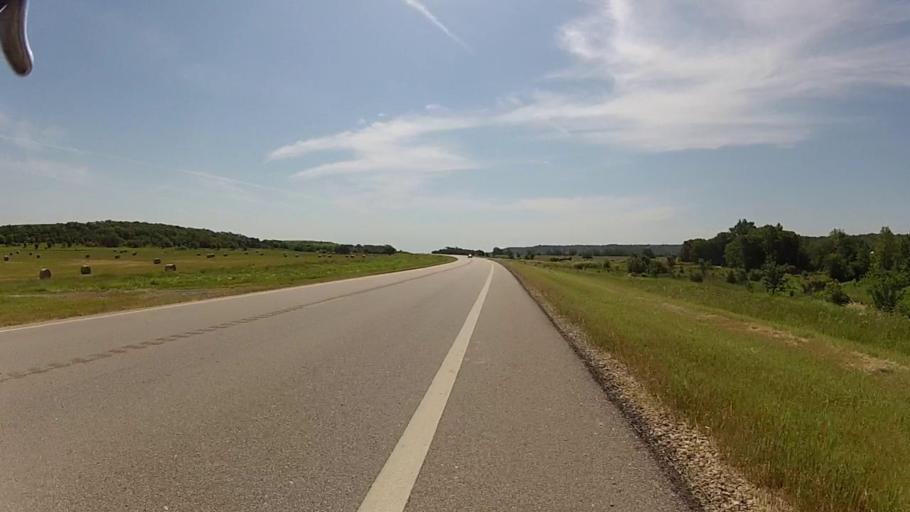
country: US
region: Kansas
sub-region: Chautauqua County
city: Sedan
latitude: 37.1081
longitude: -96.5853
